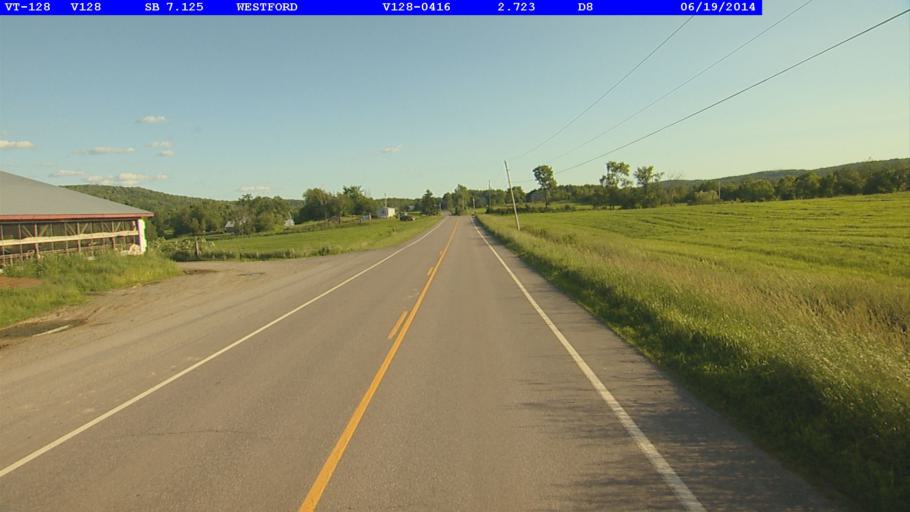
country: US
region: Vermont
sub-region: Chittenden County
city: Jericho
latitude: 44.5964
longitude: -73.0112
